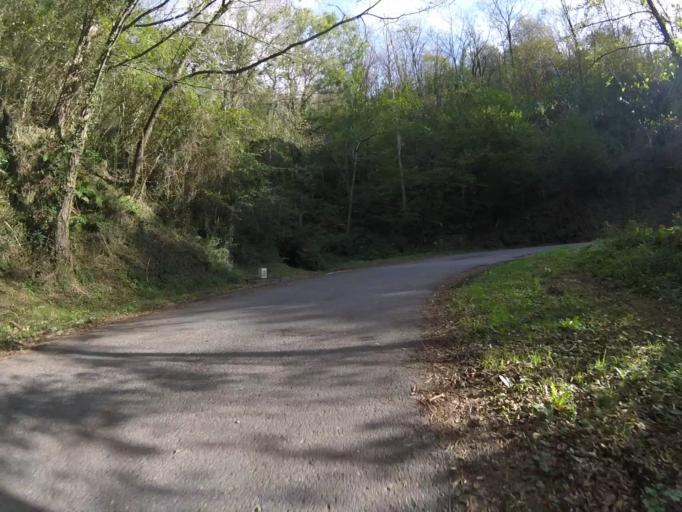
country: ES
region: Basque Country
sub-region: Provincia de Guipuzcoa
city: Orio
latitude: 43.2889
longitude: -2.1022
